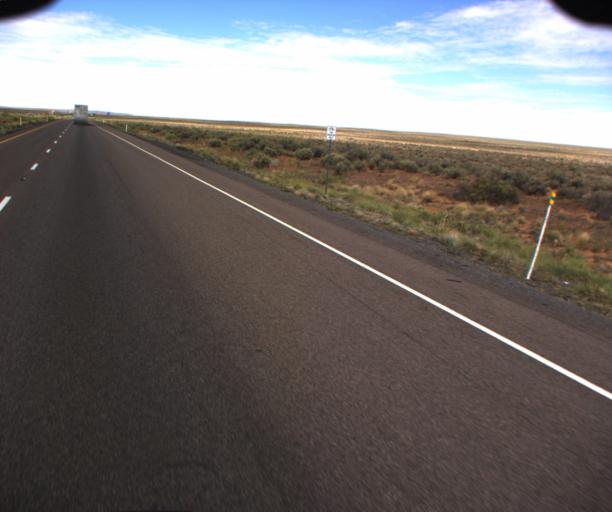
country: US
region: Arizona
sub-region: Apache County
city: Houck
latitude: 35.0991
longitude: -109.6447
